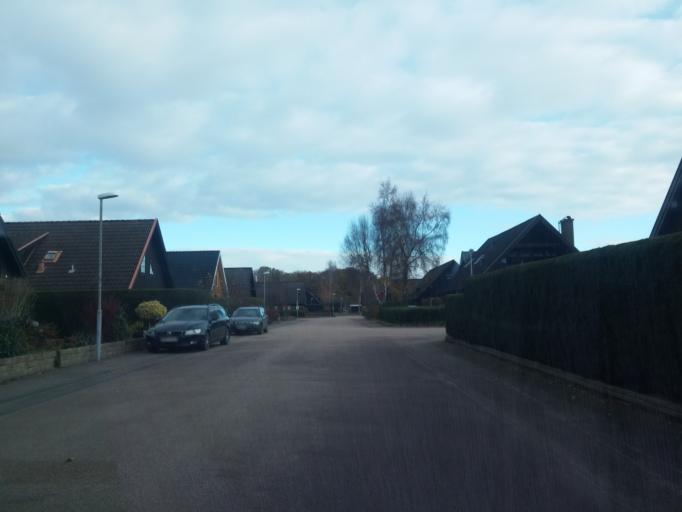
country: SE
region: Skane
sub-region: Angelholms Kommun
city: AEngelholm
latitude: 56.2313
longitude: 12.8364
